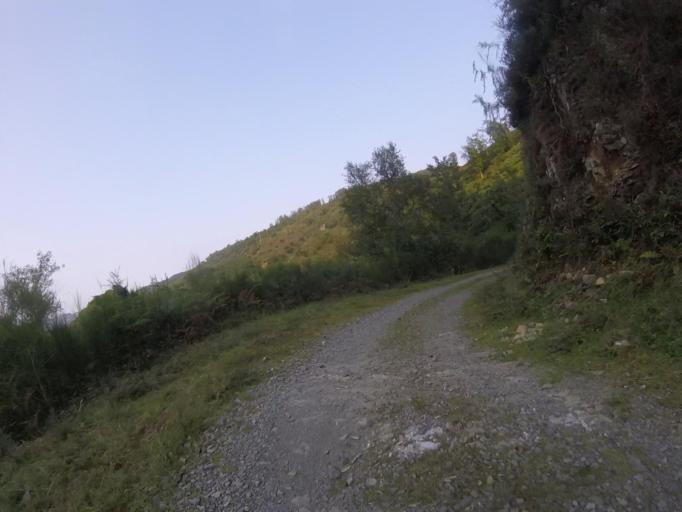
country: ES
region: Navarre
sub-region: Provincia de Navarra
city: Arano
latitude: 43.2554
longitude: -1.8469
